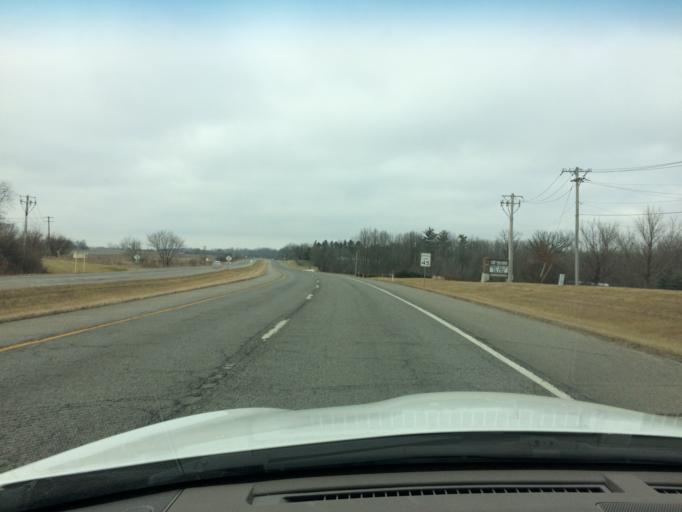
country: US
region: Illinois
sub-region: Kane County
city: Sugar Grove
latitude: 41.7792
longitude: -88.4434
